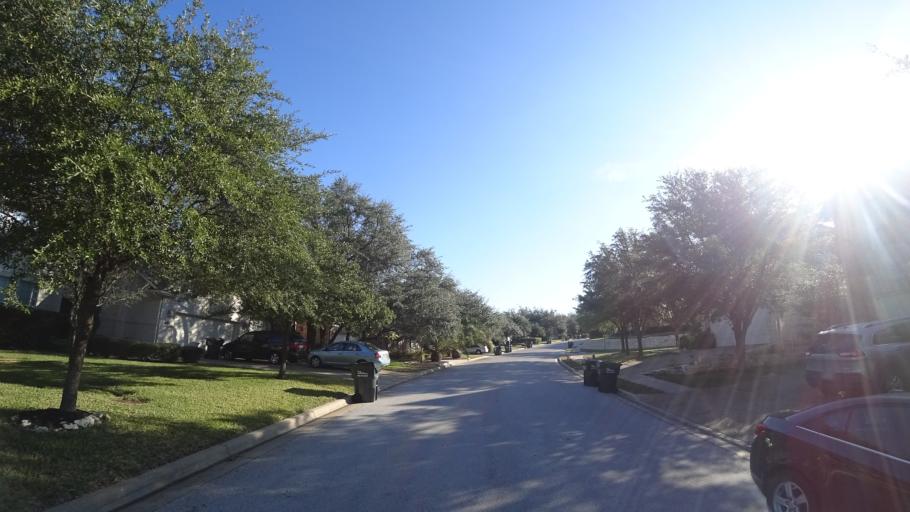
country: US
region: Texas
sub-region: Travis County
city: Hudson Bend
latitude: 30.3720
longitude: -97.9006
